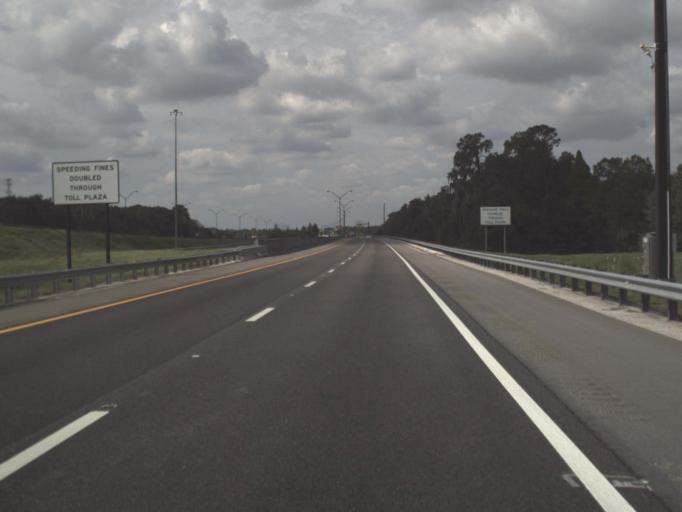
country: US
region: Florida
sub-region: Polk County
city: Fussels Corner
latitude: 28.0110
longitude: -81.8477
